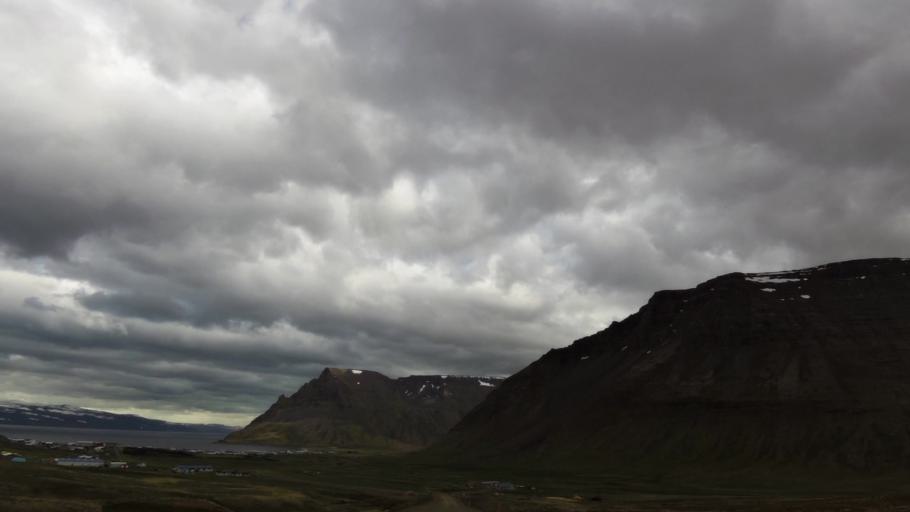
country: IS
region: Westfjords
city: Isafjoerdur
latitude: 66.1594
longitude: -23.2980
